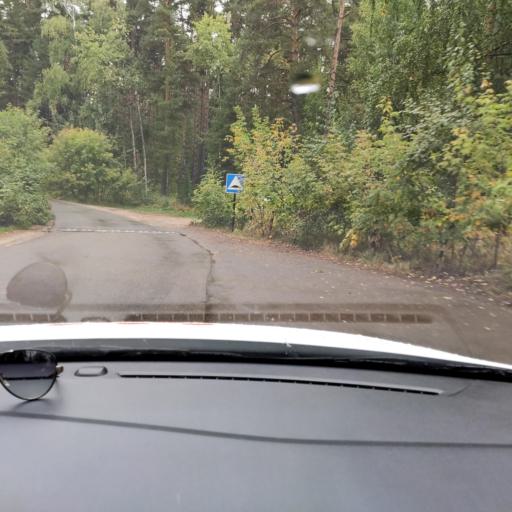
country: RU
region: Tatarstan
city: Verkhniy Uslon
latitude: 55.6426
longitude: 49.0184
